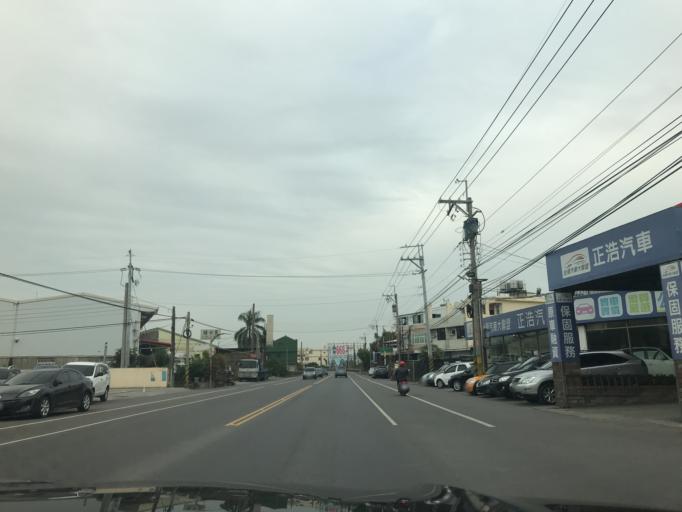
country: TW
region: Taiwan
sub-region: Nantou
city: Nantou
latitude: 23.9143
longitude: 120.5847
